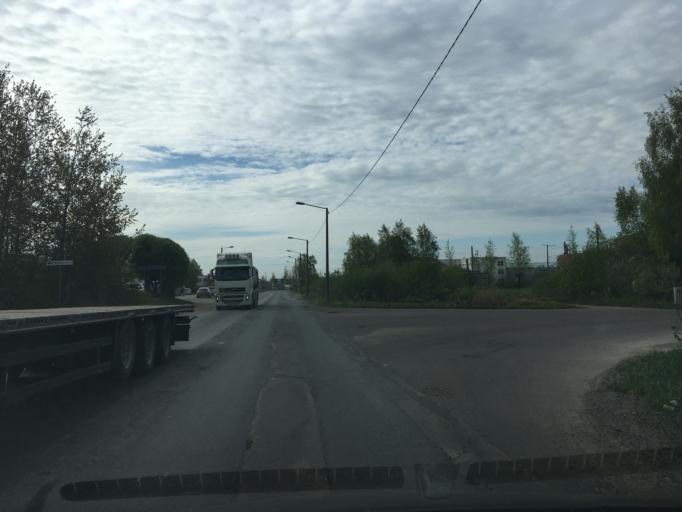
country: EE
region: Harju
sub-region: Tallinna linn
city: Kose
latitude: 59.4292
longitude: 24.8689
